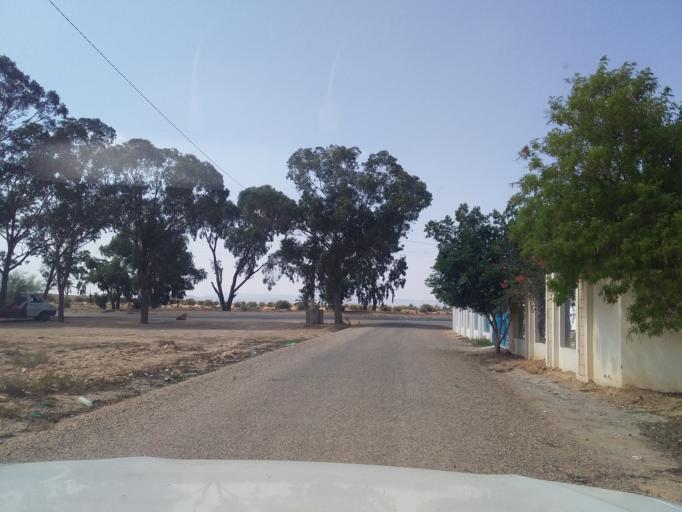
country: TN
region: Madanin
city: Medenine
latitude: 33.6037
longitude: 10.3057
